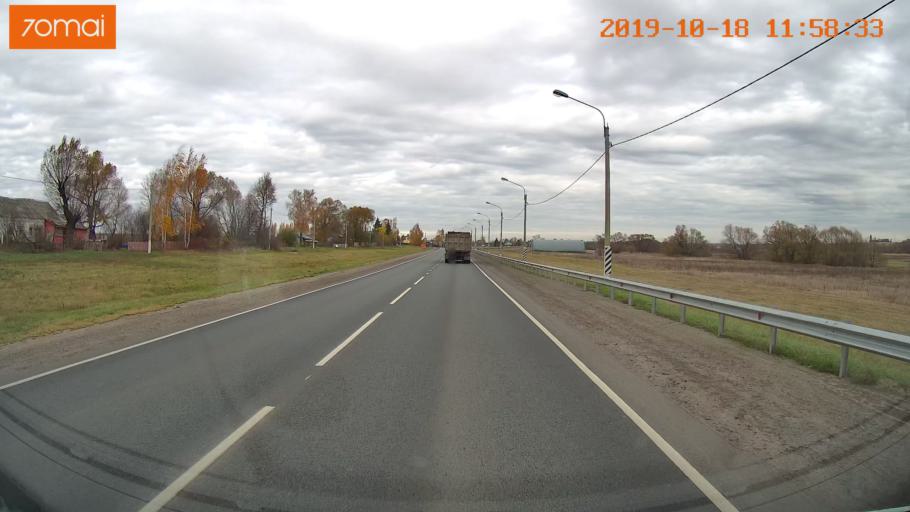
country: RU
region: Rjazan
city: Zakharovo
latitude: 54.2731
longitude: 39.1682
